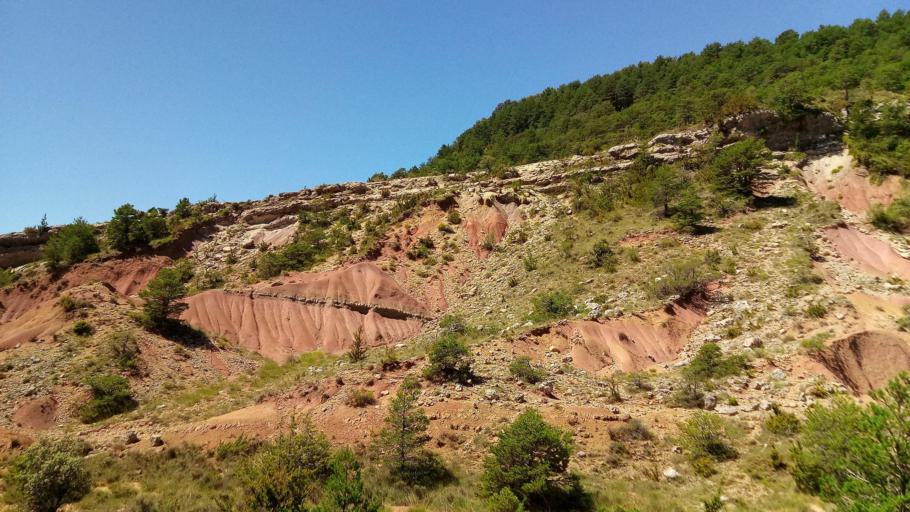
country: ES
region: Aragon
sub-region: Provincia de Huesca
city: Castigaleu
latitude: 42.3388
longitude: 0.5327
